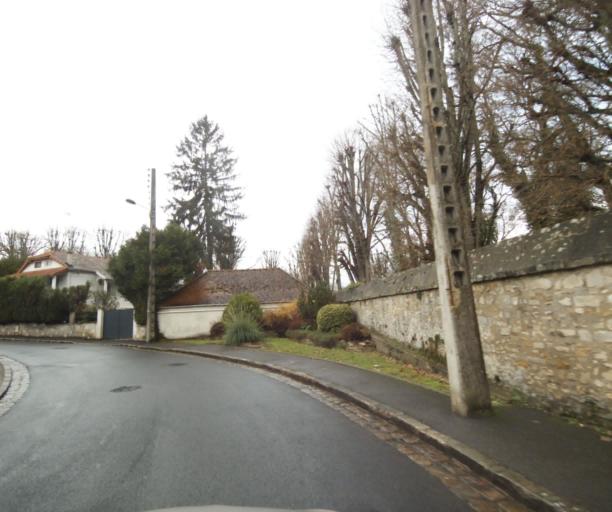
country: FR
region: Ile-de-France
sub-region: Departement de Seine-et-Marne
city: Avon
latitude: 48.4052
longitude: 2.7180
